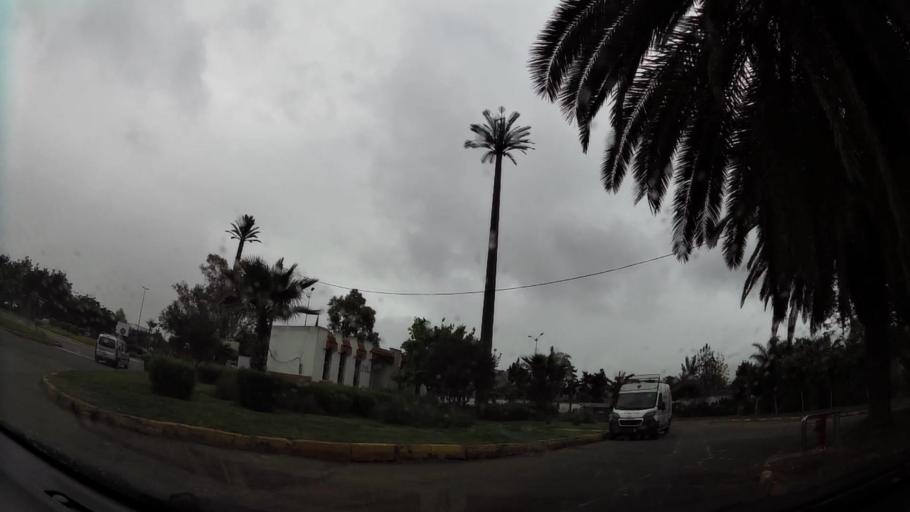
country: MA
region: Grand Casablanca
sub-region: Casablanca
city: Casablanca
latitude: 33.5313
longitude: -7.6295
